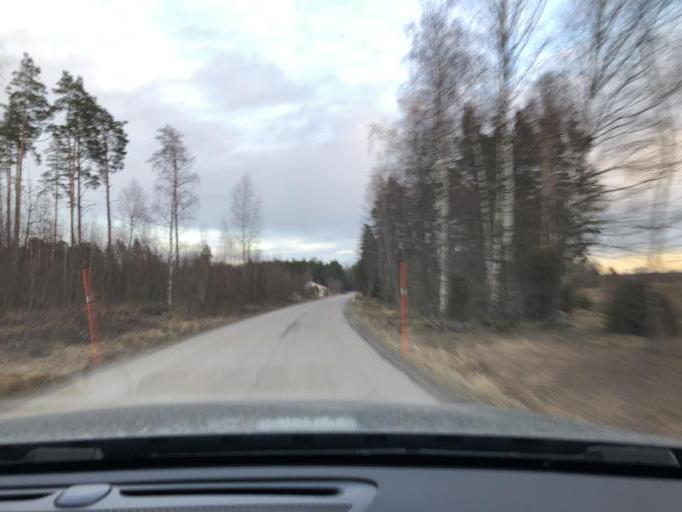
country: SE
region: Uppsala
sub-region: Uppsala Kommun
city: Gamla Uppsala
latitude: 59.9230
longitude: 17.6585
